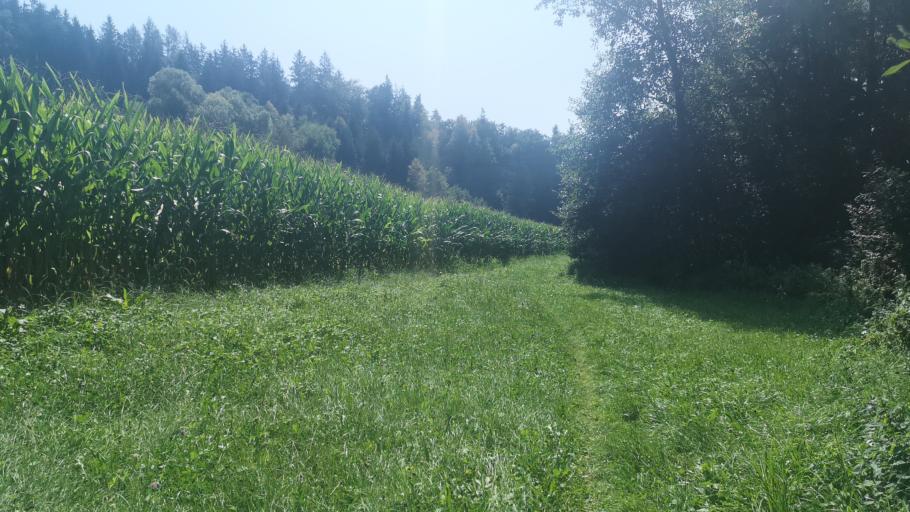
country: AT
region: Styria
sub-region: Politischer Bezirk Deutschlandsberg
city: Lannach
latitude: 46.9397
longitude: 15.3369
